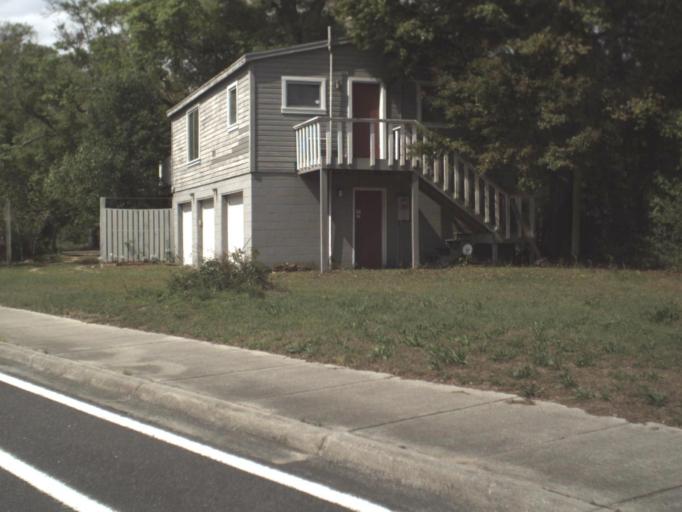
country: US
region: Florida
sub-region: Escambia County
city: Warrington
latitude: 30.3969
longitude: -87.2511
